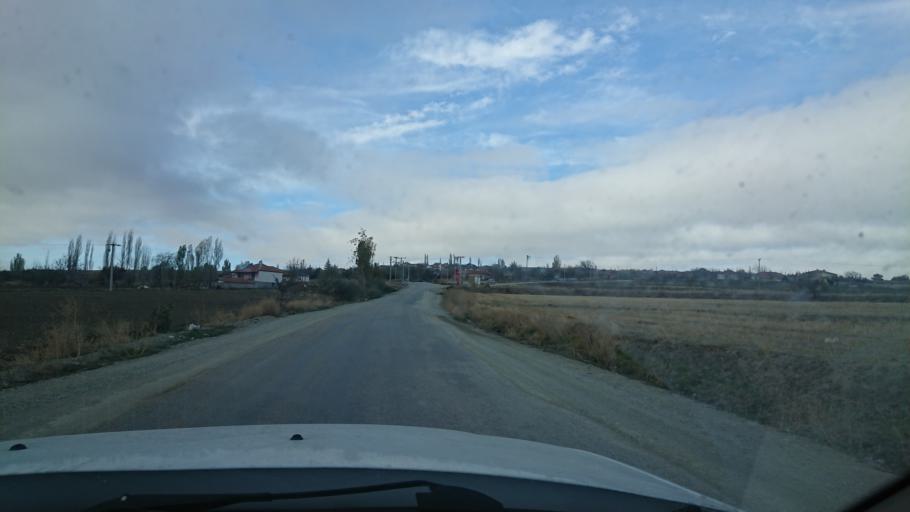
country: TR
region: Aksaray
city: Ortakoy
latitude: 38.7553
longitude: 34.0166
